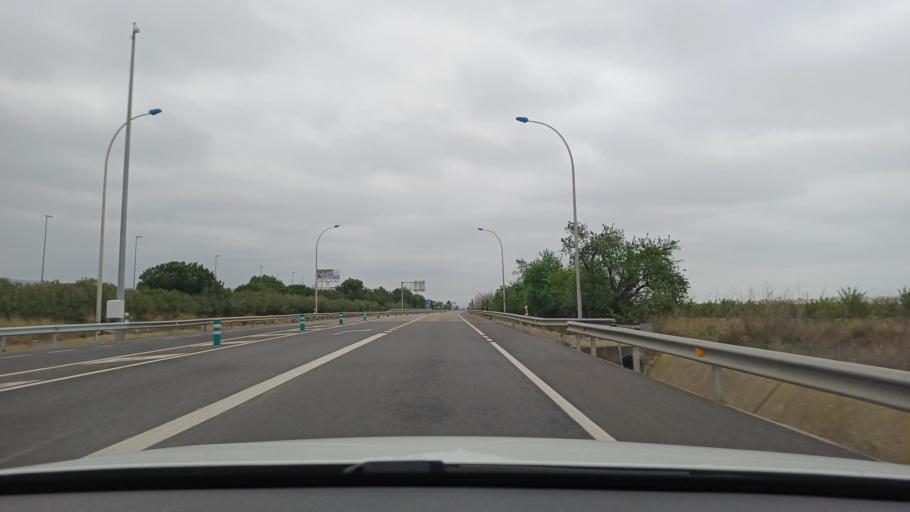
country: ES
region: Valencia
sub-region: Provincia de Castello
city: Orpesa/Oropesa del Mar
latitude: 40.1044
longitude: 0.1362
